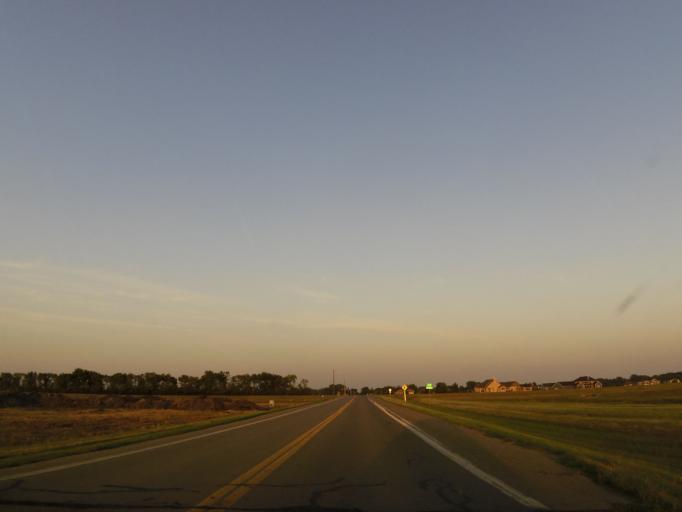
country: US
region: North Dakota
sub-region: Grand Forks County
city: Grand Forks
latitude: 47.8603
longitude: -97.0271
